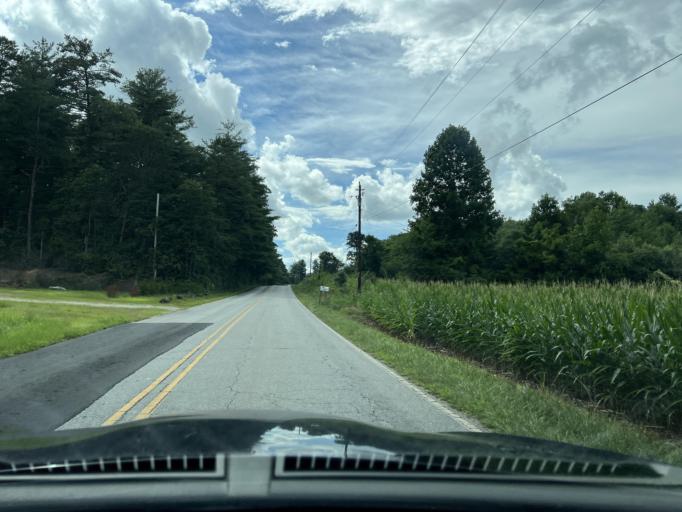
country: US
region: North Carolina
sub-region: Henderson County
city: Fruitland
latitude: 35.3922
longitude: -82.3753
